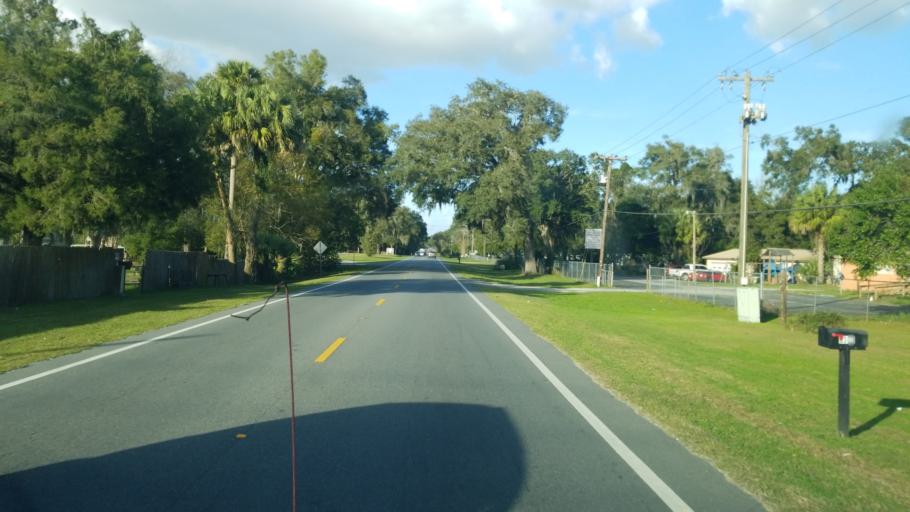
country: US
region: Florida
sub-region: Marion County
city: Ocala
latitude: 29.2523
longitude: -82.1157
